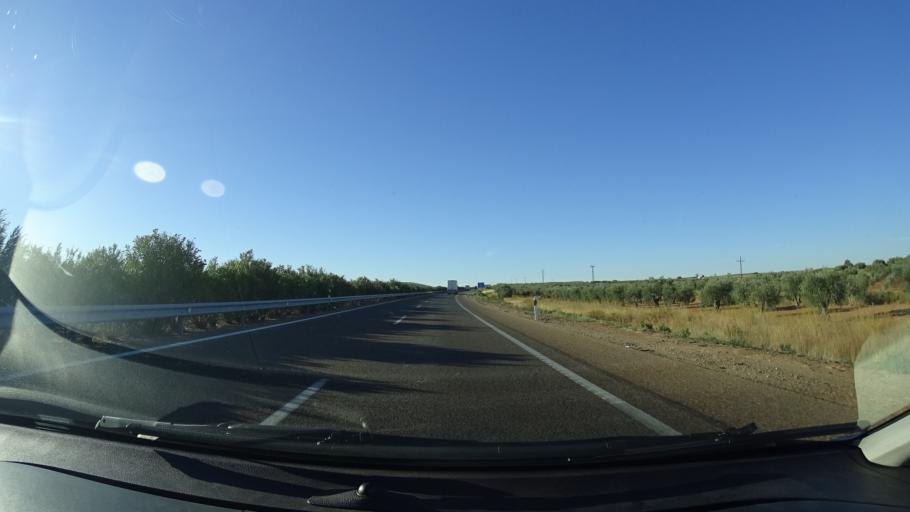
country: ES
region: Extremadura
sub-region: Provincia de Badajoz
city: Los Santos de Maimona
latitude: 38.4894
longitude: -6.3554
